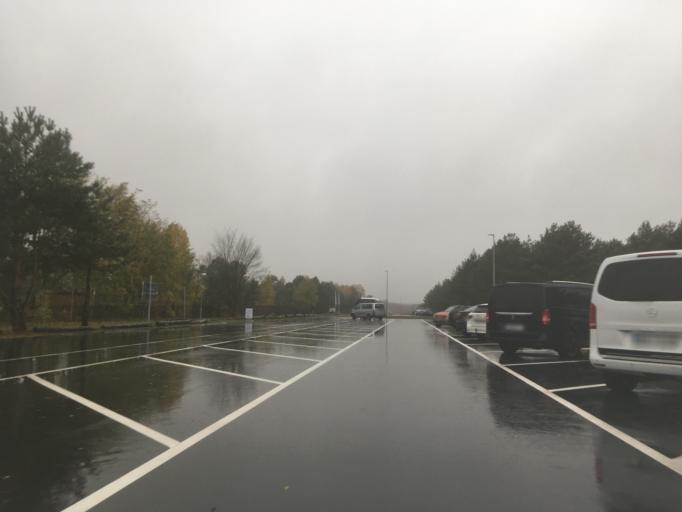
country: DE
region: Brandenburg
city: Halbe
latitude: 52.0332
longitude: 13.7396
